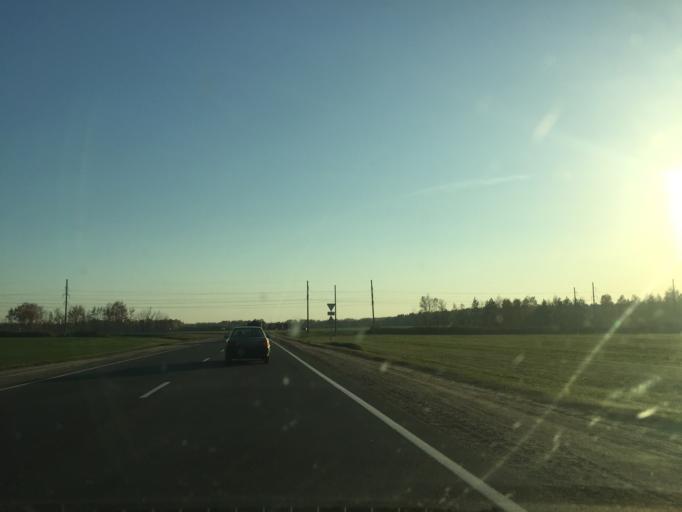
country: BY
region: Mogilev
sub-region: Mahilyowski Rayon
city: Kadino
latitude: 53.8686
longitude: 30.4833
